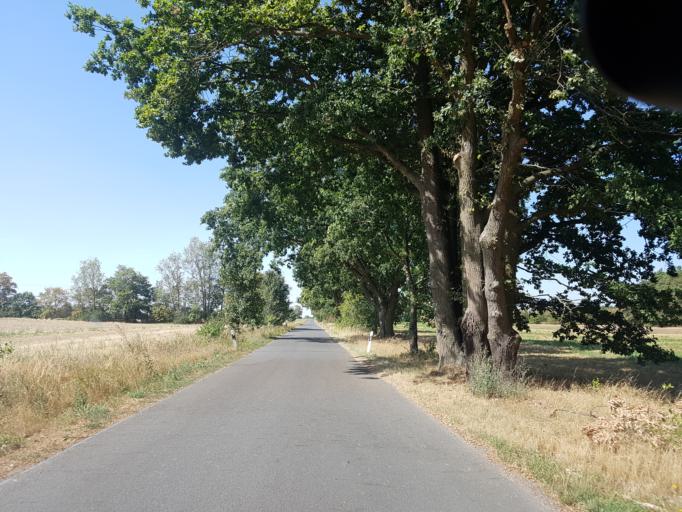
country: DE
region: Saxony-Anhalt
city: Kropstadt
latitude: 52.0325
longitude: 12.7878
